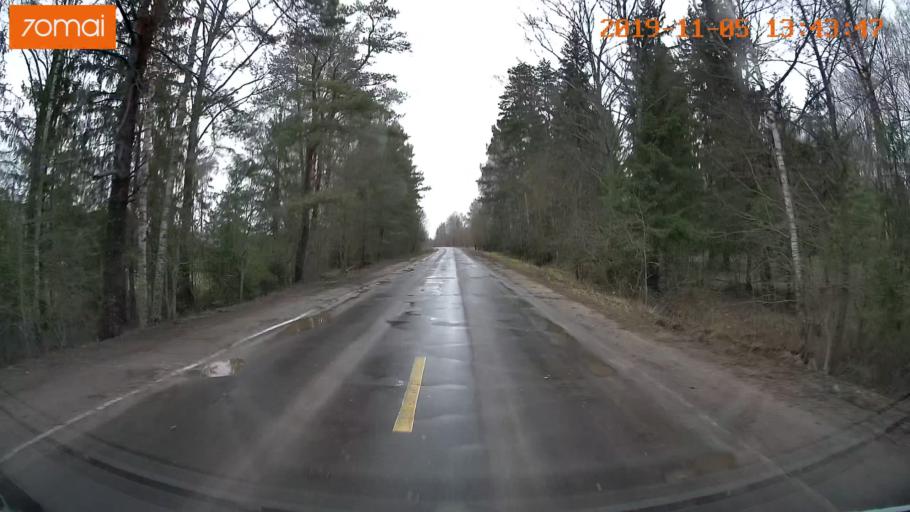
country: RU
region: Ivanovo
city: Shuya
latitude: 56.9761
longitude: 41.4057
